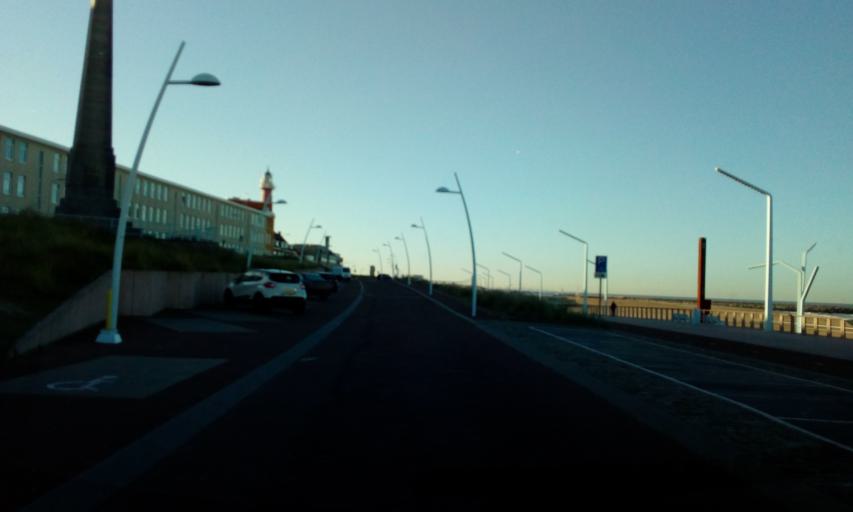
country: NL
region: South Holland
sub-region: Gemeente Den Haag
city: Scheveningen
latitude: 52.1063
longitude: 4.2700
